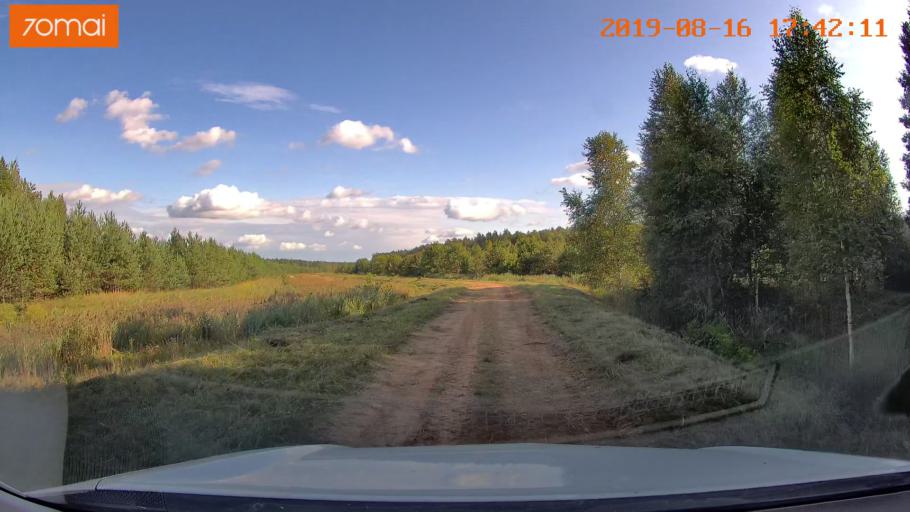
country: BY
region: Mogilev
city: Asipovichy
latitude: 53.2374
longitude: 28.6652
